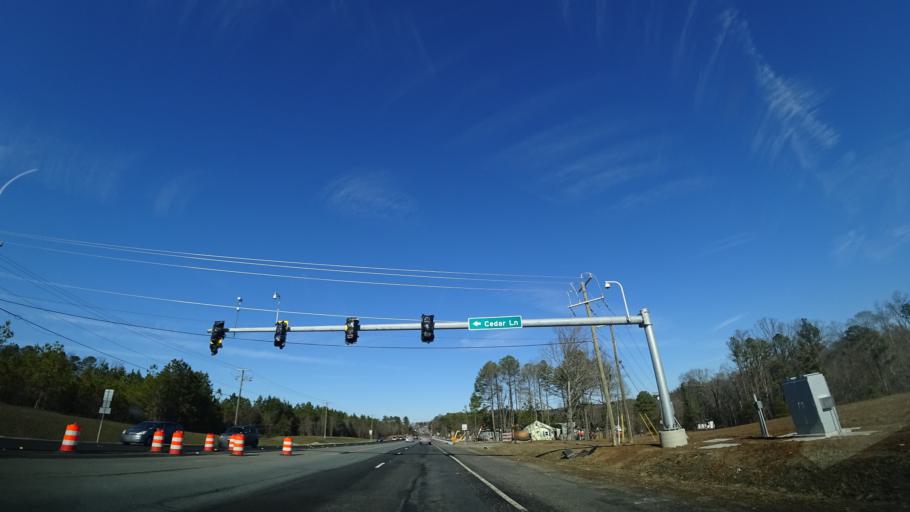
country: US
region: Virginia
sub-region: Henrico County
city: Glen Allen
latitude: 37.6906
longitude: -77.4627
